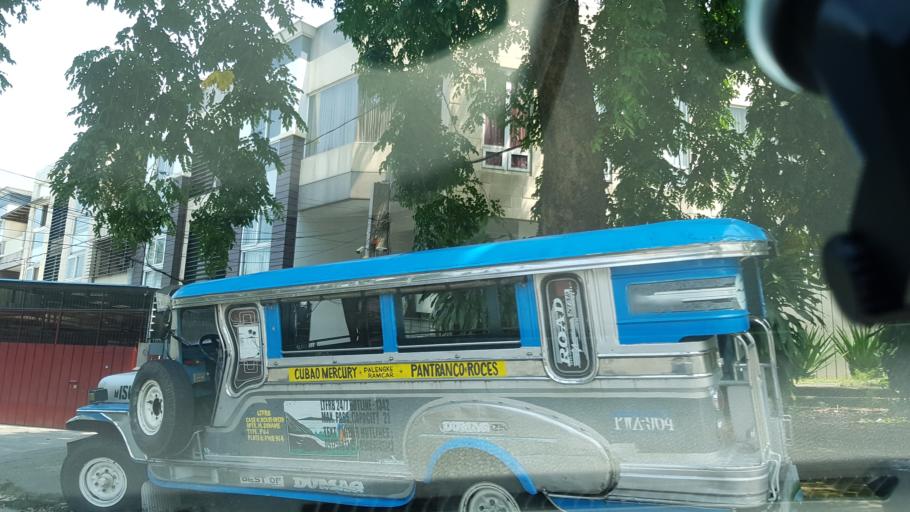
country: PH
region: Calabarzon
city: Del Monte
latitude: 14.6299
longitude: 121.0187
